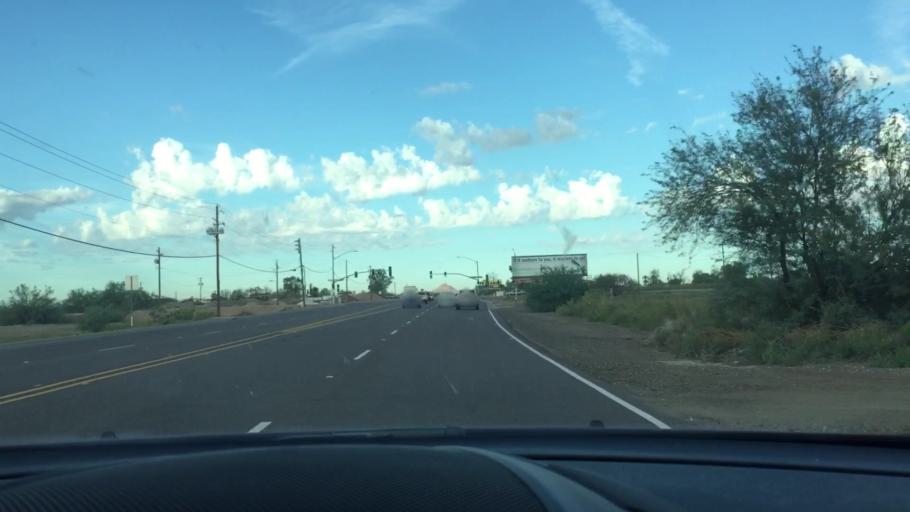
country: US
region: Arizona
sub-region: Maricopa County
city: Mesa
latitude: 33.4640
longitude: -111.8531
